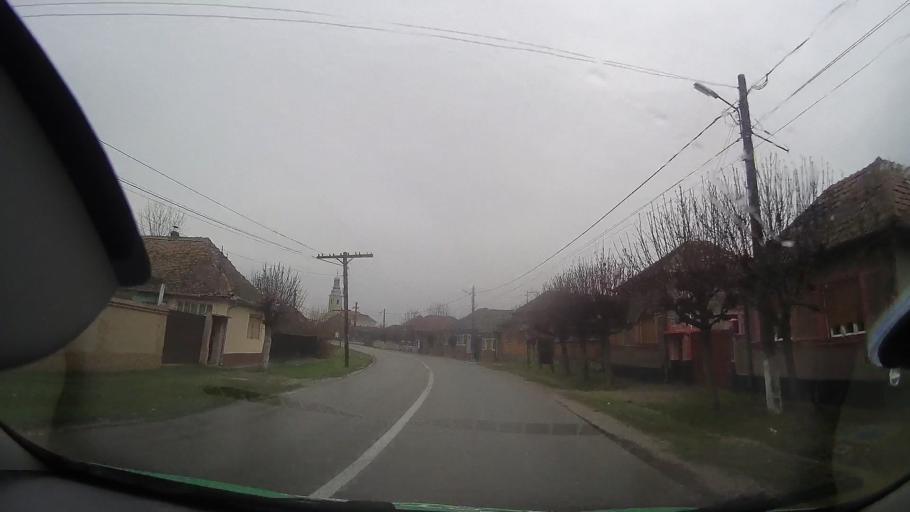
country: RO
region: Bihor
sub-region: Comuna Tinca
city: Gurbediu
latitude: 46.7882
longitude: 21.8673
